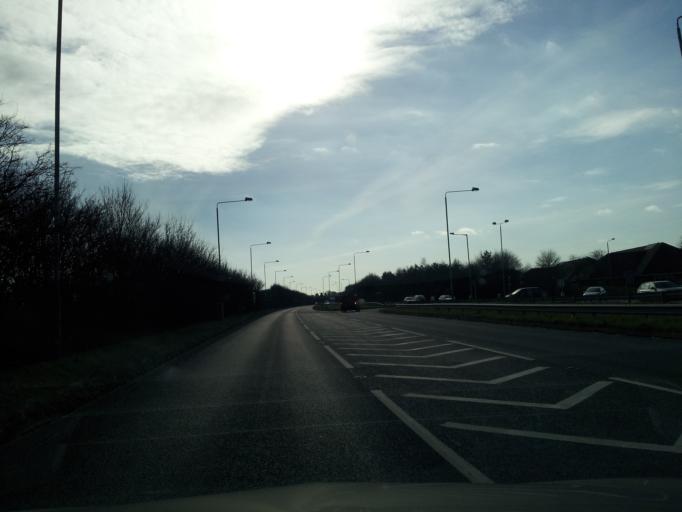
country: GB
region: England
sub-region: Nottinghamshire
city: West Bridgford
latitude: 52.9236
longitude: -1.0983
